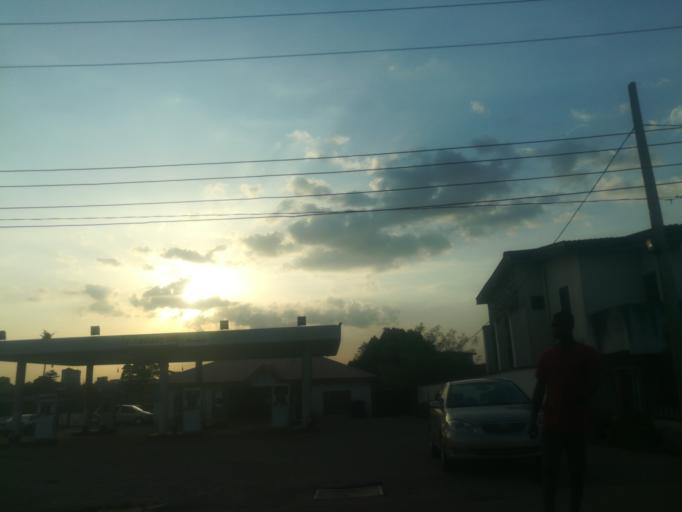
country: NG
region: Ogun
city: Abeokuta
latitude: 7.1425
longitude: 3.3381
